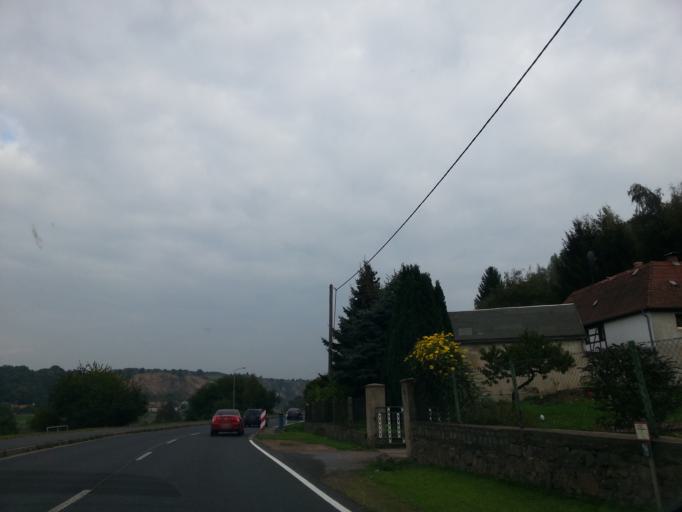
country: DE
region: Saxony
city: Meissen
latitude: 51.1879
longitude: 13.4332
